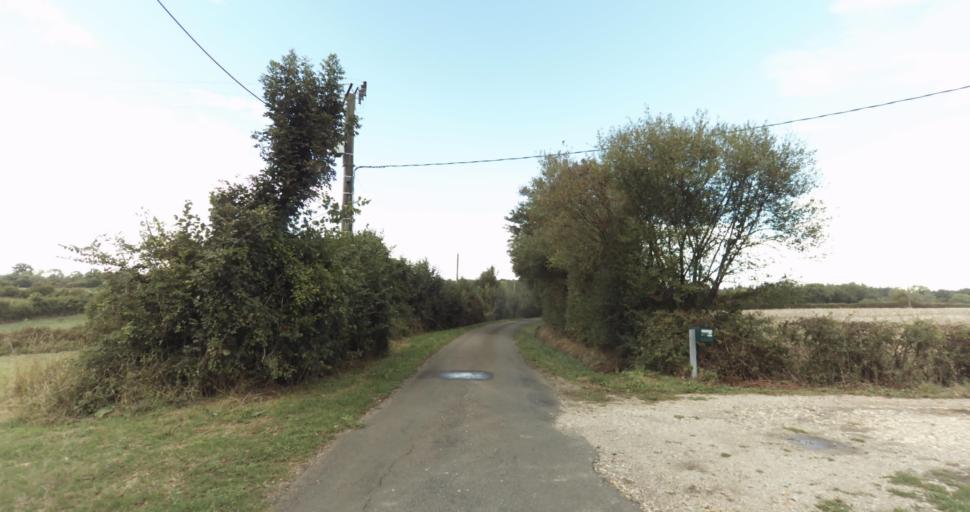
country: FR
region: Lower Normandy
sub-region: Departement de l'Orne
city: Sainte-Gauburge-Sainte-Colombe
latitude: 48.7480
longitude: 0.4098
